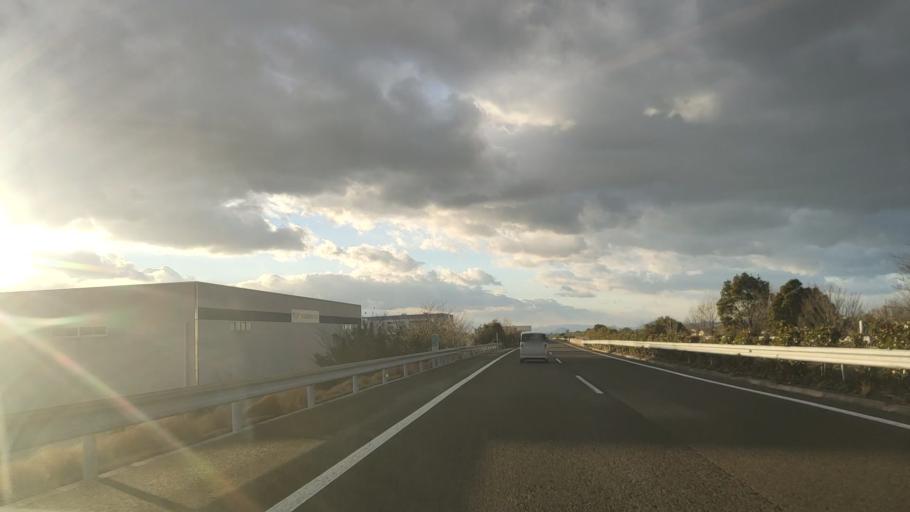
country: JP
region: Ehime
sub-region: Shikoku-chuo Shi
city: Matsuyama
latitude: 33.7851
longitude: 132.8456
